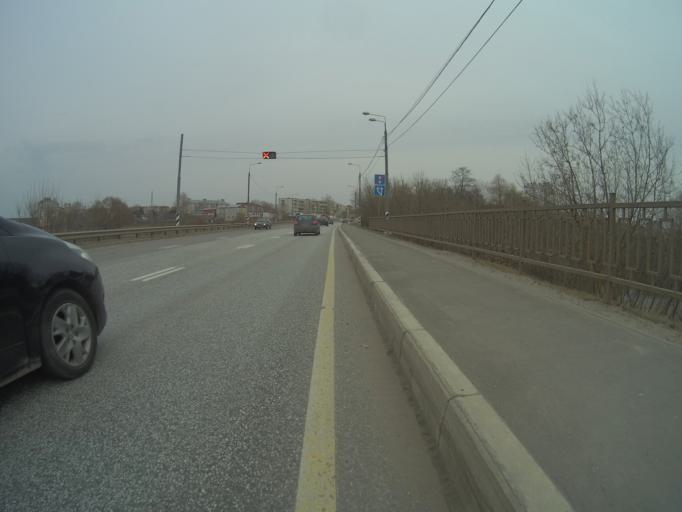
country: RU
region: Vladimir
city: Kommunar
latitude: 56.1124
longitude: 40.4263
